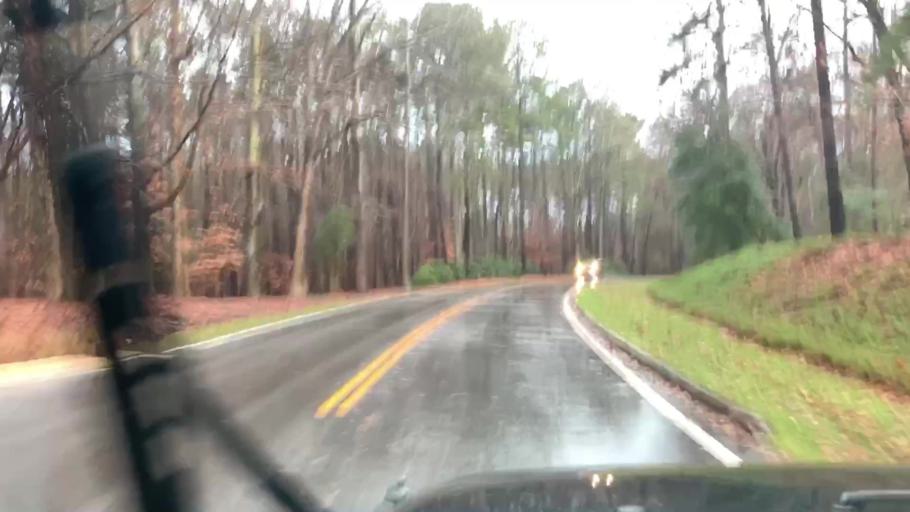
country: US
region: Virginia
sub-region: City of Williamsburg
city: Williamsburg
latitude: 37.2391
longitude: -76.6611
